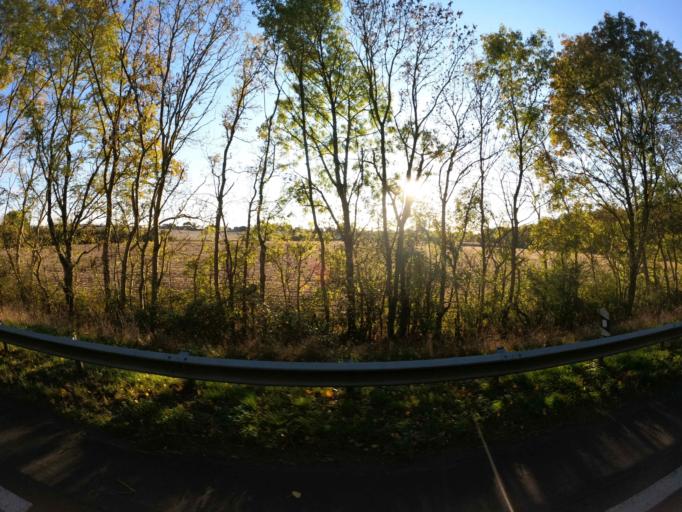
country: FR
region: Pays de la Loire
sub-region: Departement de la Vendee
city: Sainte-Hermine
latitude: 46.5561
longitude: -1.0433
